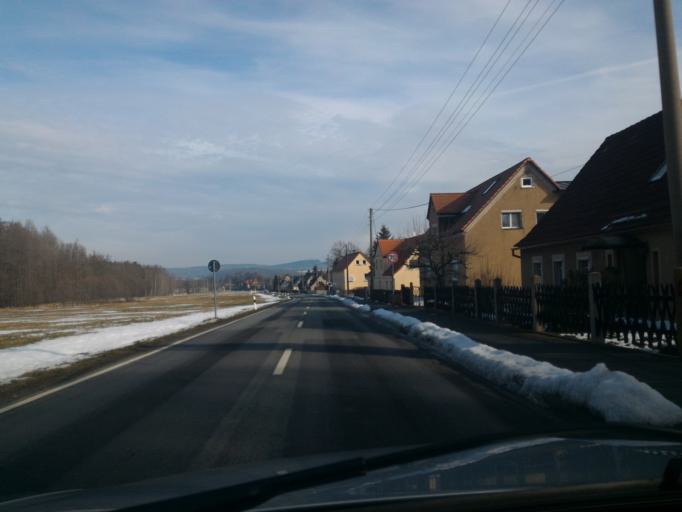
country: DE
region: Saxony
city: Grossschonau
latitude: 50.8788
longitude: 14.6581
